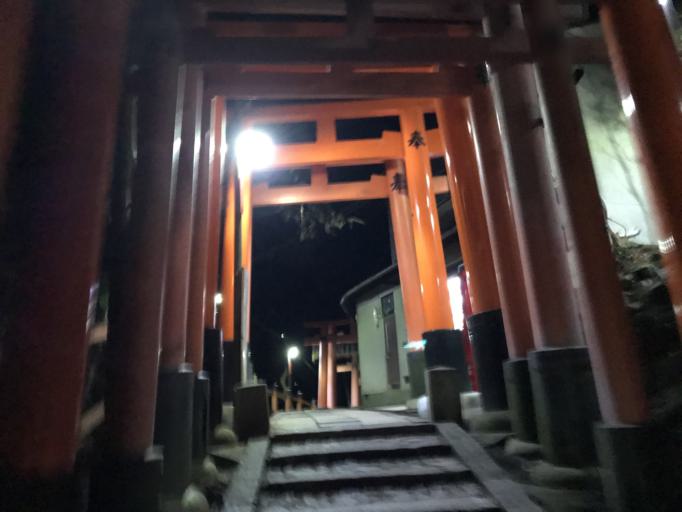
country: JP
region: Kyoto
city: Kyoto
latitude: 34.9696
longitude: 135.7847
